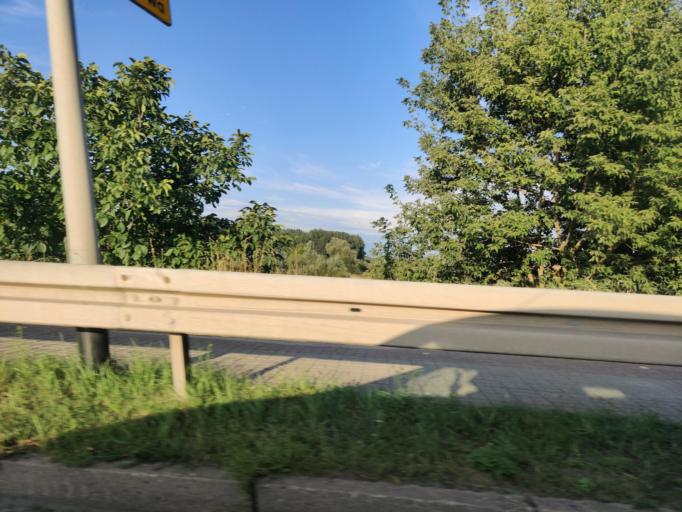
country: PL
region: Greater Poland Voivodeship
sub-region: Konin
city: Konin
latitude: 52.2215
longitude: 18.2518
